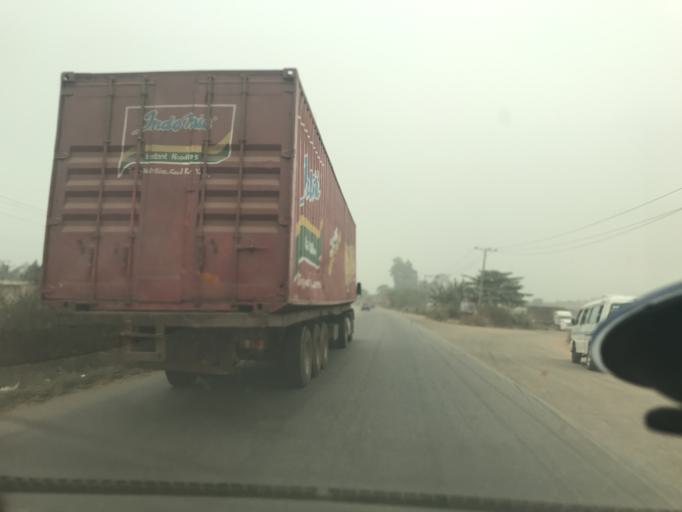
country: NG
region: Ogun
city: Shagamu
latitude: 6.8672
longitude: 3.6061
